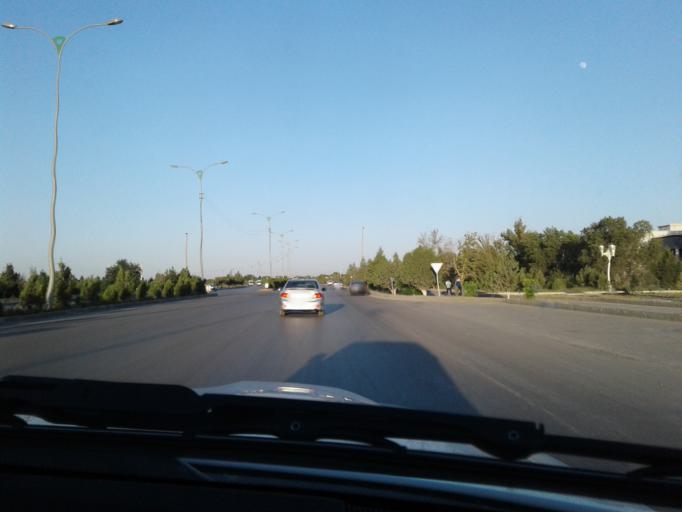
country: TM
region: Ahal
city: Abadan
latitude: 38.1621
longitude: 57.9484
